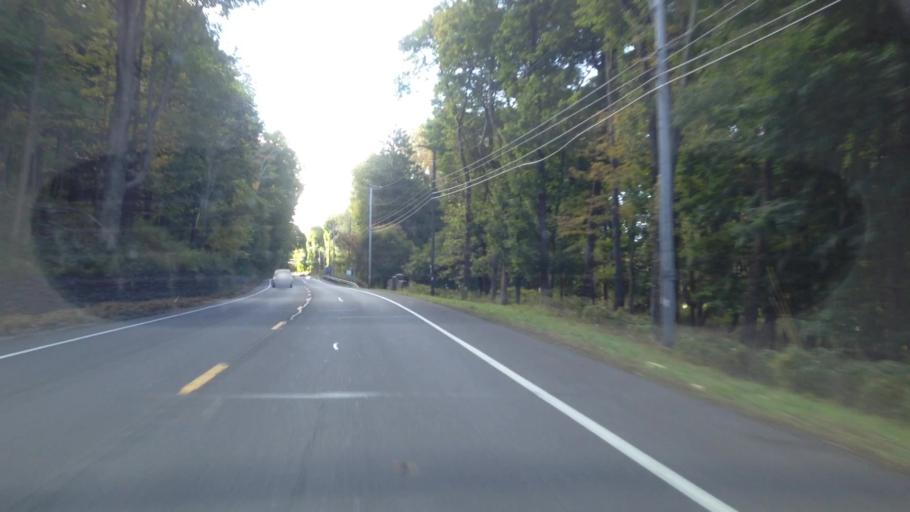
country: US
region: New York
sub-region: Dutchess County
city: Hyde Park
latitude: 41.8149
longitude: -73.9640
